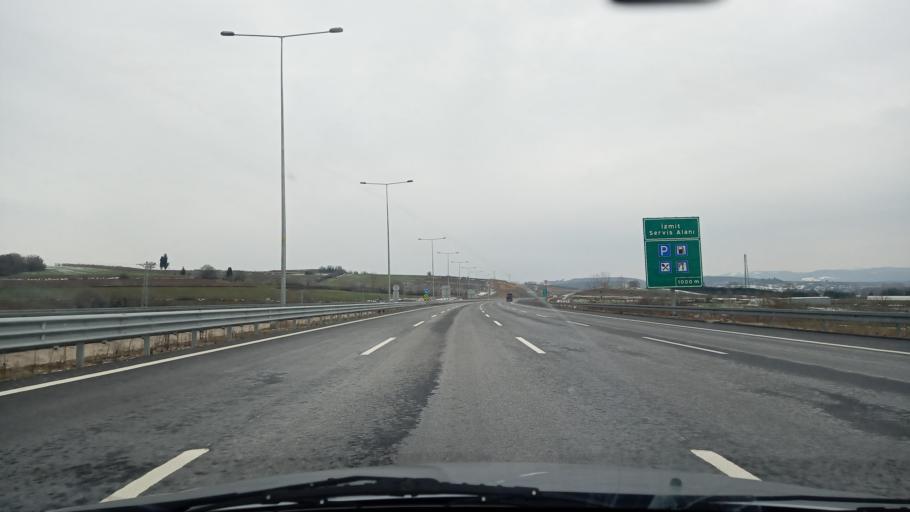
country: TR
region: Kocaeli
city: Kosekoy
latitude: 40.7963
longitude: 30.0590
